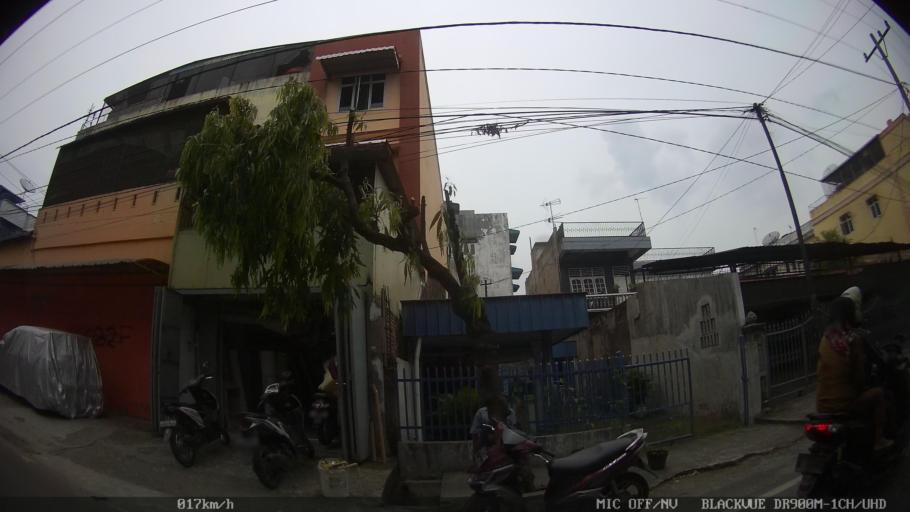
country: ID
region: North Sumatra
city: Medan
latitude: 3.5820
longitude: 98.7023
